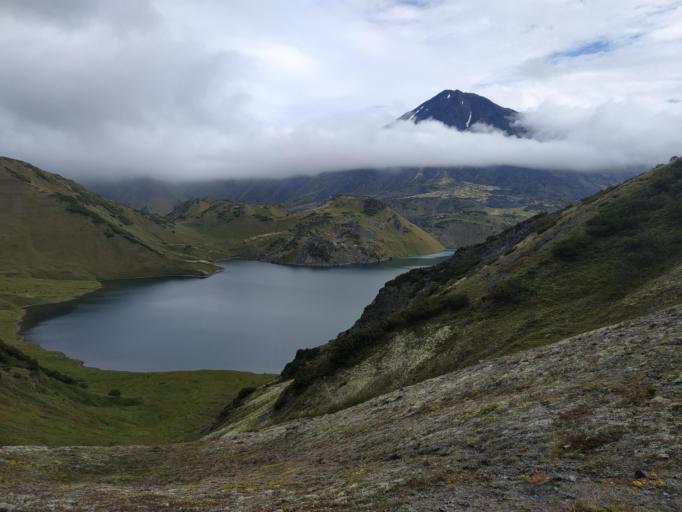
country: RU
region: Kamtsjatka
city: Yelizovo
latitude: 53.8709
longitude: 158.0267
